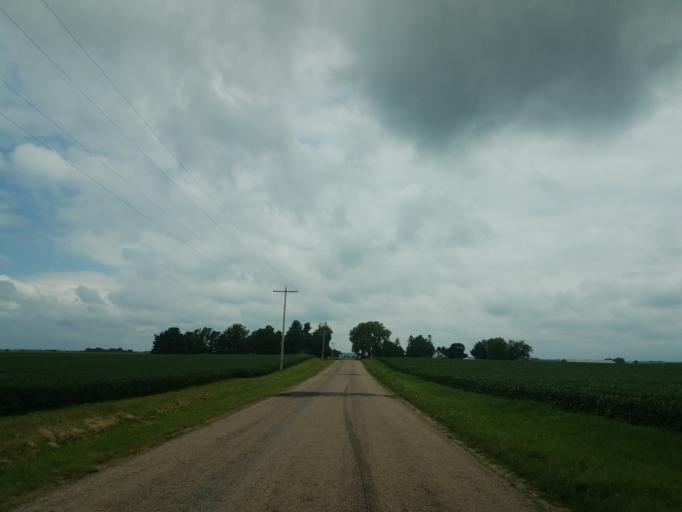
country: US
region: Illinois
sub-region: McLean County
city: Twin Grove
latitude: 40.4124
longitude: -89.0621
